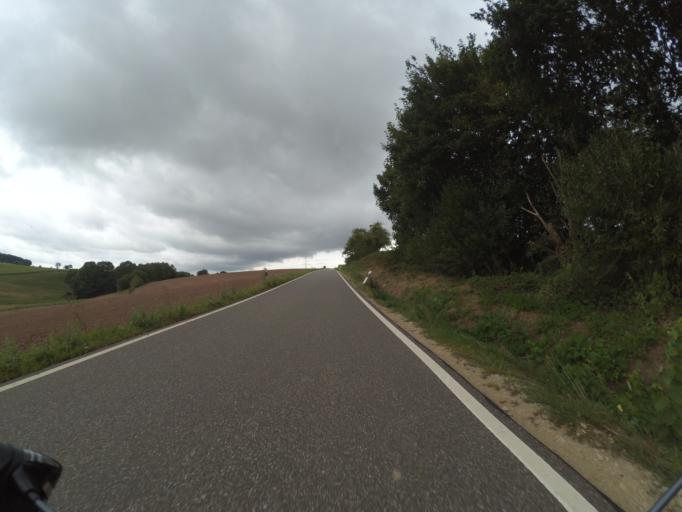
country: DE
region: Rheinland-Pfalz
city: Zemmer
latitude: 49.8974
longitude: 6.6874
